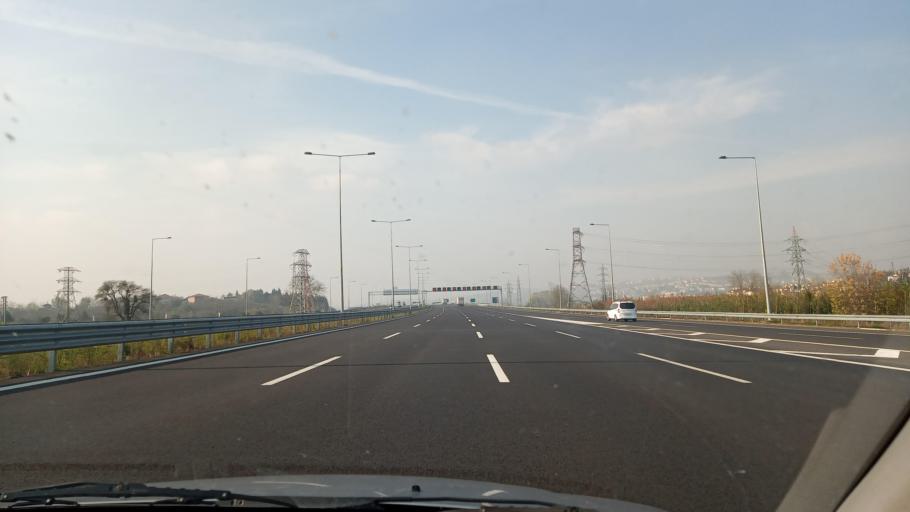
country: TR
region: Sakarya
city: Kazimpasa
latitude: 40.8435
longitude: 30.3396
